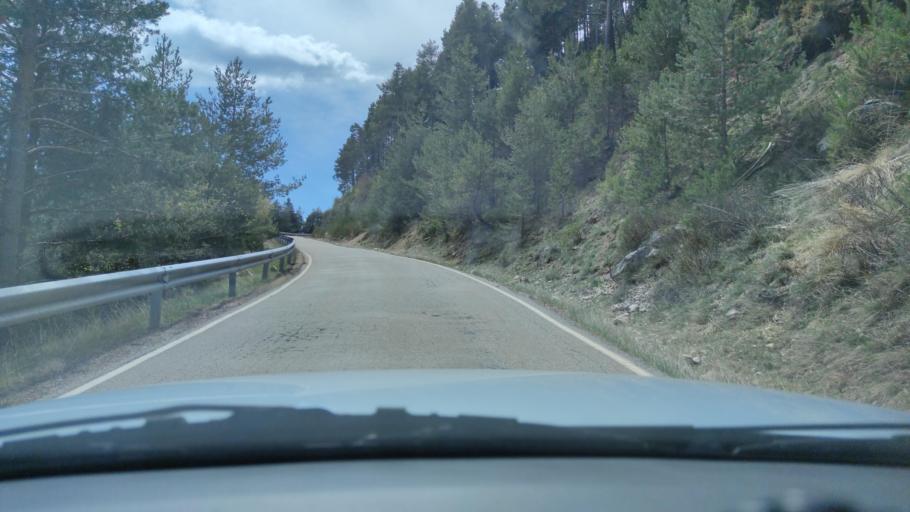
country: ES
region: Catalonia
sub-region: Provincia de Lleida
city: Gosol
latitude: 42.1994
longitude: 1.5634
